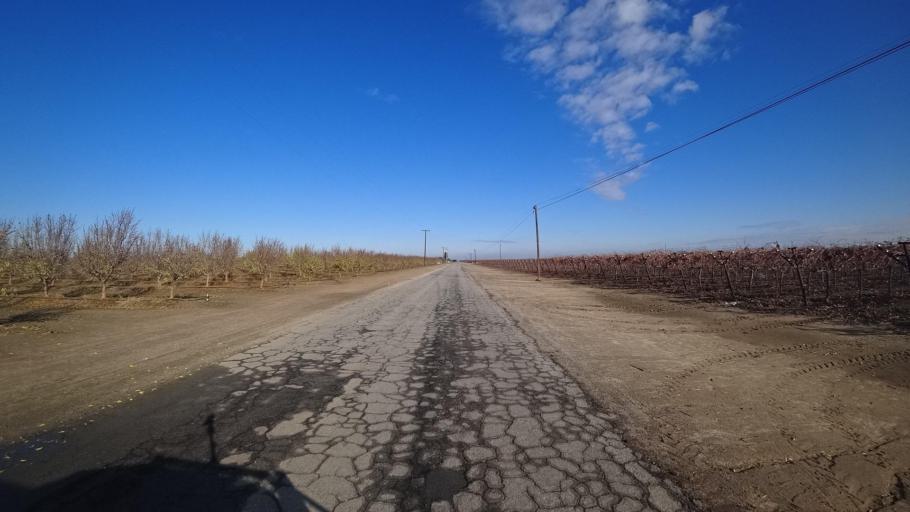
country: US
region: California
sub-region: Kern County
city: Delano
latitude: 35.7228
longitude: -119.3030
